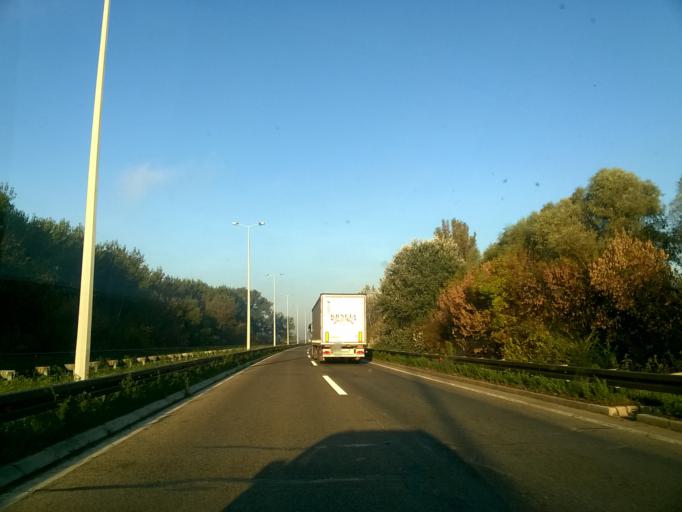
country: RS
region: Autonomna Pokrajina Vojvodina
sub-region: Juznobanatski Okrug
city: Pancevo
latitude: 44.8591
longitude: 20.5980
